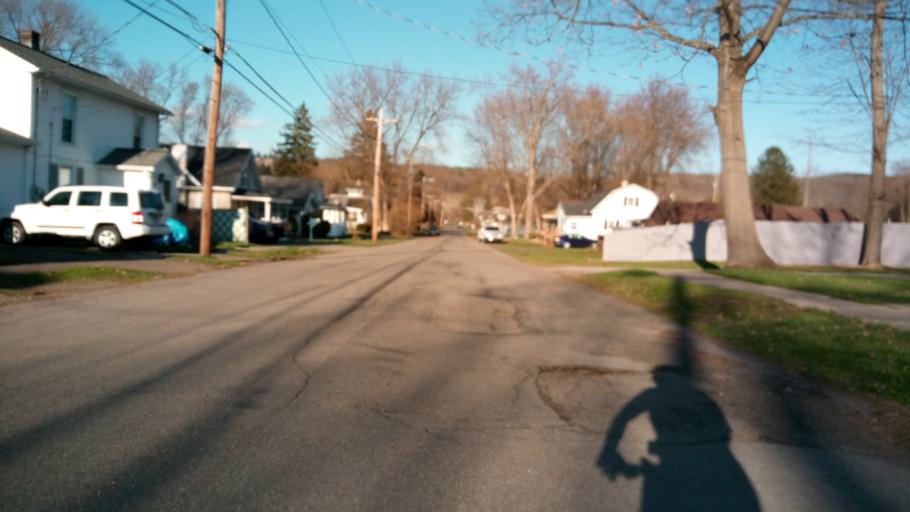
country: US
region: New York
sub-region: Chemung County
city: Elmira
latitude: 42.0769
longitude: -76.7854
